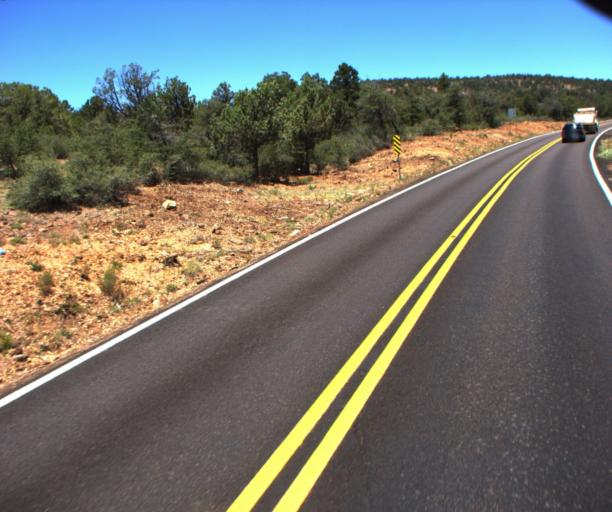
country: US
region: Arizona
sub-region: Gila County
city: Pine
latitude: 34.3432
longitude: -111.4258
